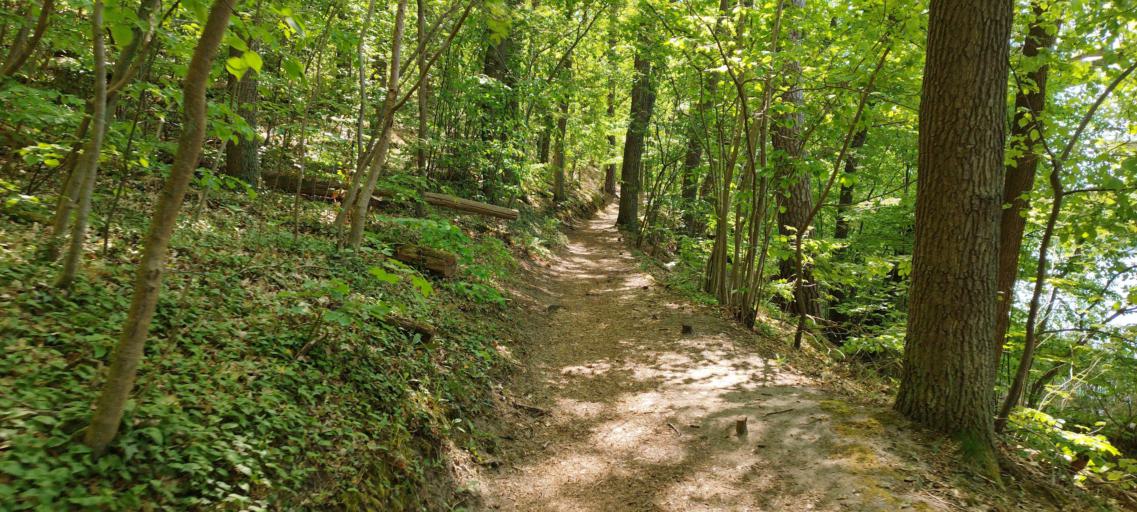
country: DE
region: Brandenburg
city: Furstenwalde
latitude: 52.3968
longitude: 14.0402
